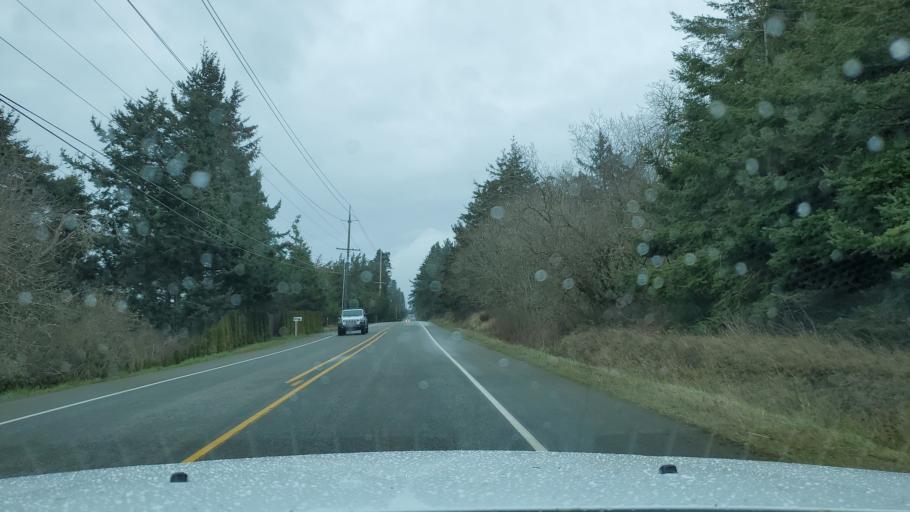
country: US
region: Washington
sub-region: Island County
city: Coupeville
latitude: 48.2690
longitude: -122.7421
